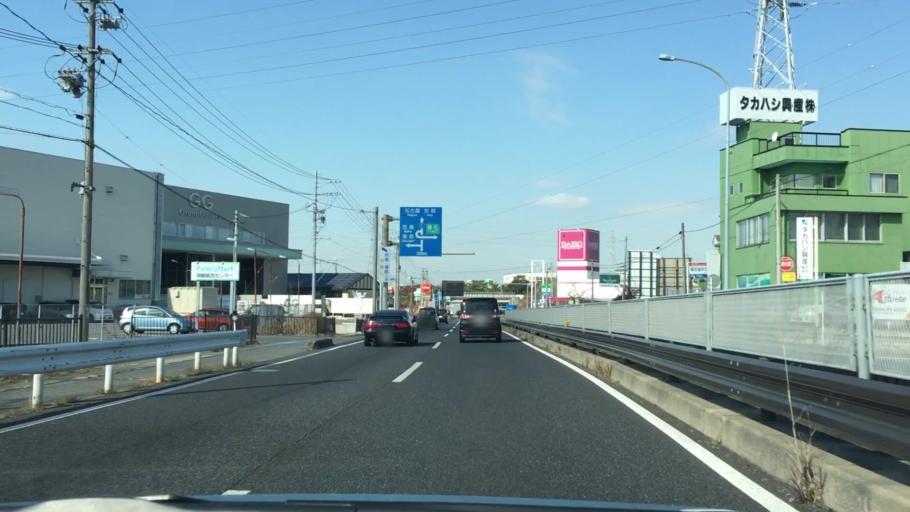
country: JP
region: Aichi
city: Okazaki
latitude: 34.9424
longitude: 137.1916
